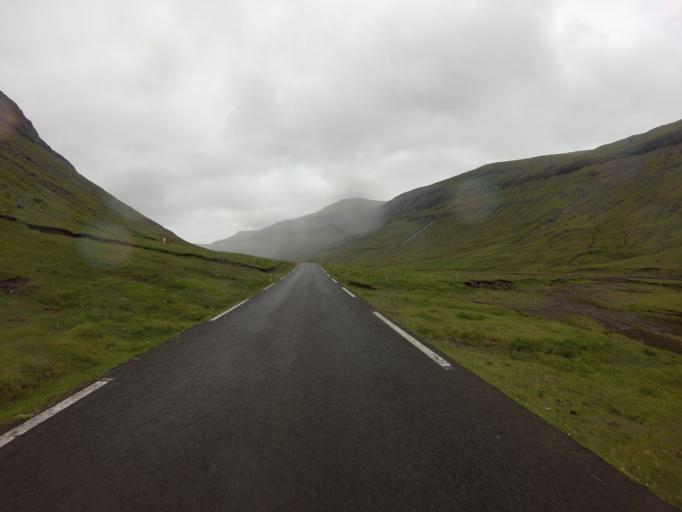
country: FO
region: Streymoy
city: Vestmanna
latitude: 62.2300
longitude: -7.1363
